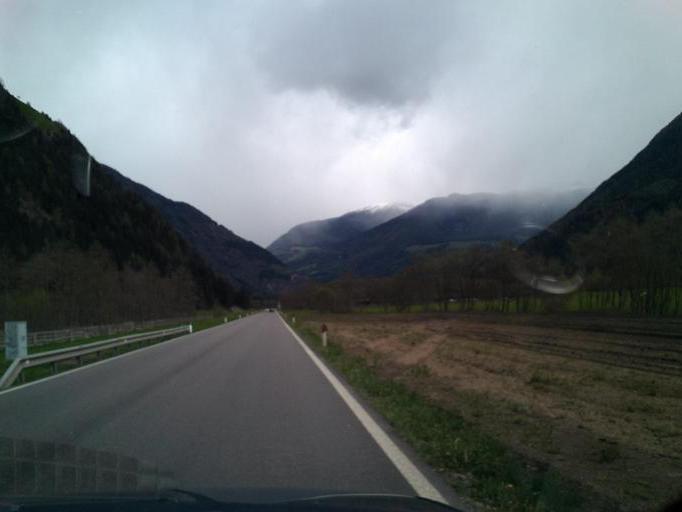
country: IT
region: Trentino-Alto Adige
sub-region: Bolzano
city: Molini di Tures
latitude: 46.8753
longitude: 11.9480
